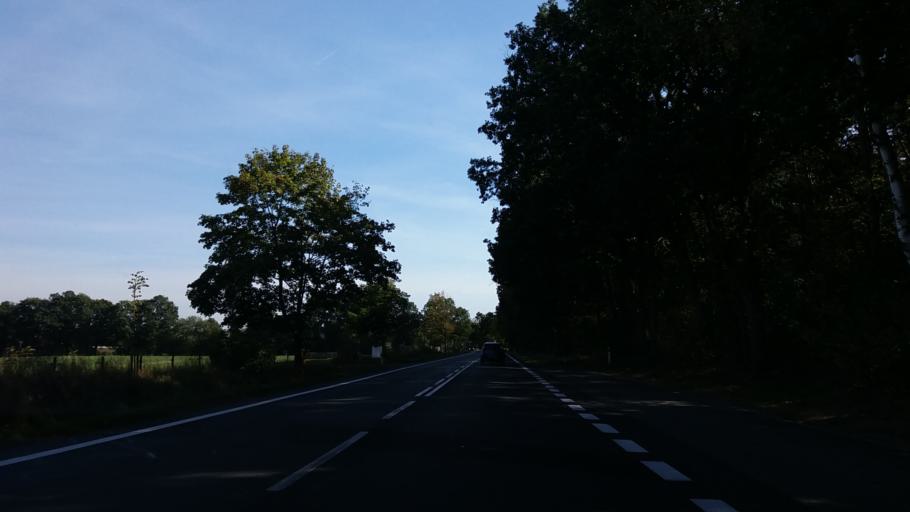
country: PL
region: Greater Poland Voivodeship
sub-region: Powiat miedzychodzki
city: Kwilcz
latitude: 52.5394
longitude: 16.1385
